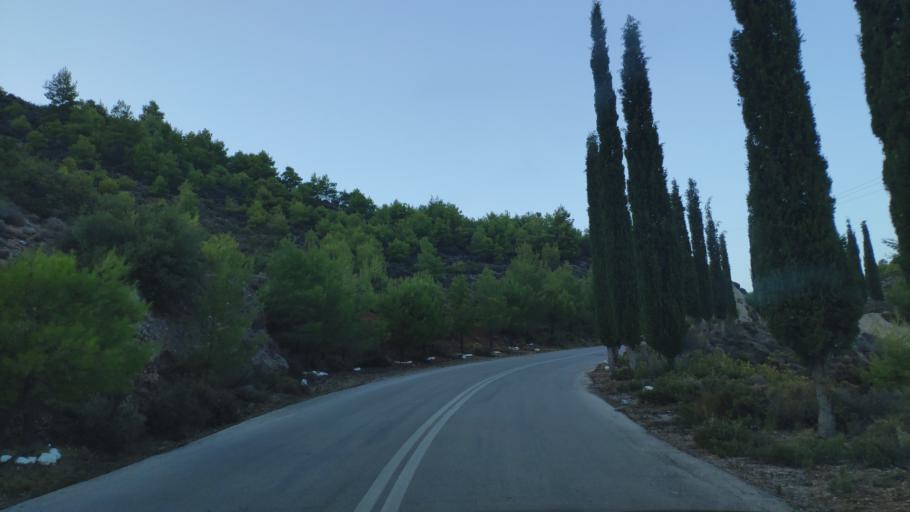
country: GR
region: West Greece
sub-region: Nomos Achaias
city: Aiyira
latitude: 38.0903
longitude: 22.4076
